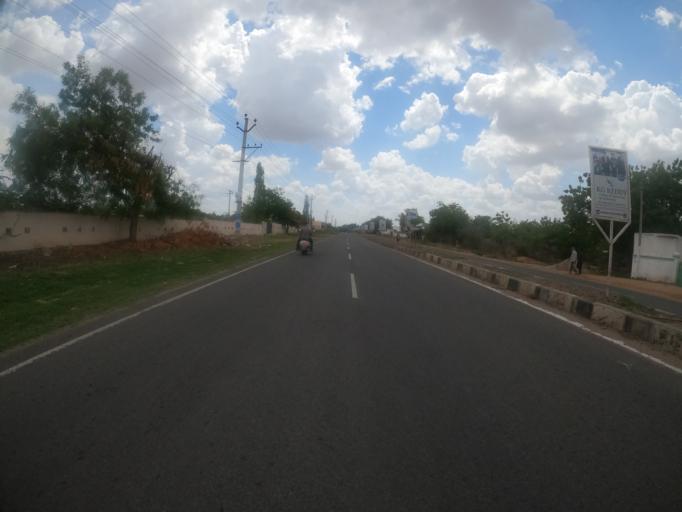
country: IN
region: Telangana
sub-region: Rangareddi
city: Sriramnagar
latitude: 17.3311
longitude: 78.2920
